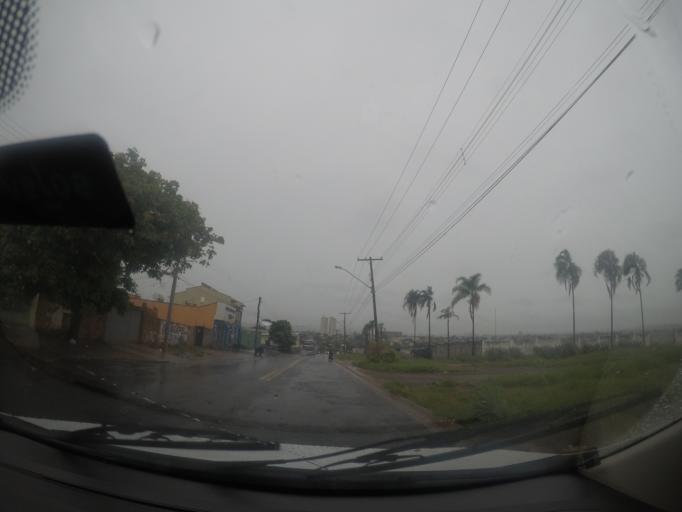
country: BR
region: Goias
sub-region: Goiania
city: Goiania
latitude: -16.6566
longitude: -49.3150
